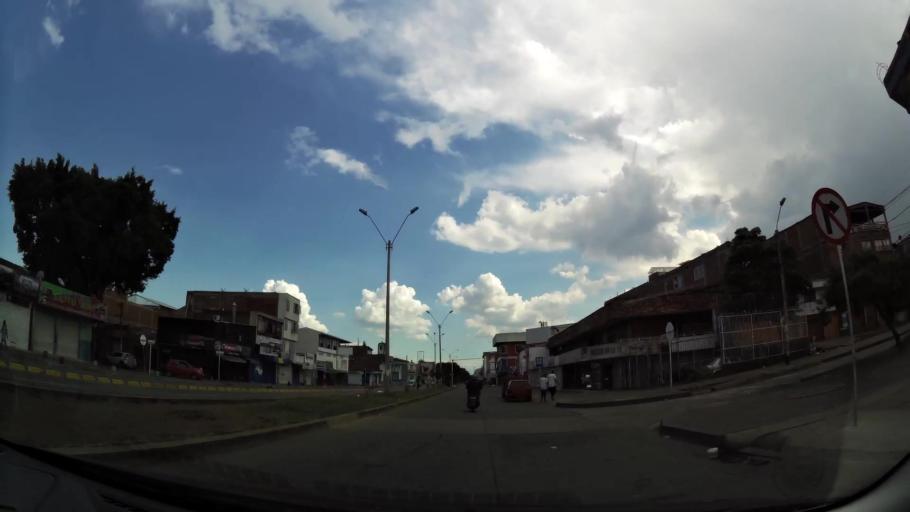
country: CO
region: Valle del Cauca
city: Cali
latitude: 3.4422
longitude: -76.5261
